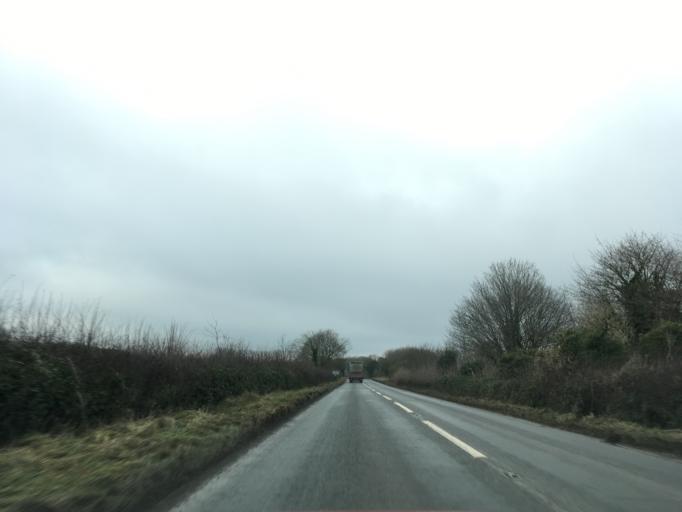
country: GB
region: England
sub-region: Gloucestershire
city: Tetbury
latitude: 51.6546
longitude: -2.1300
